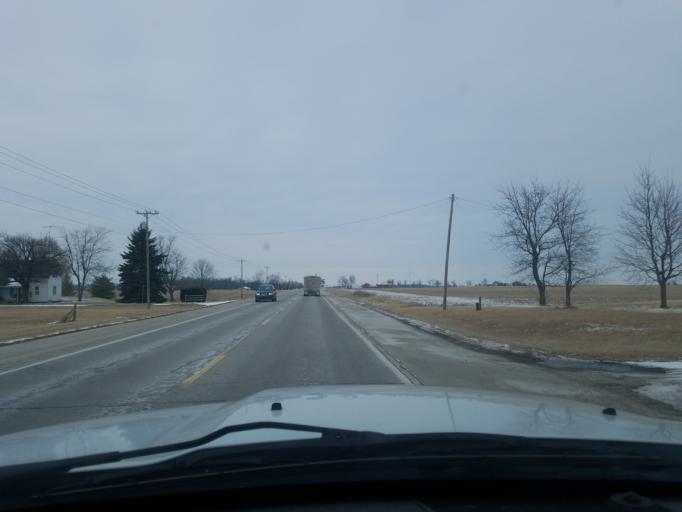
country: US
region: Indiana
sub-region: Randolph County
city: Lynn
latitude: 40.0667
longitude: -84.9397
